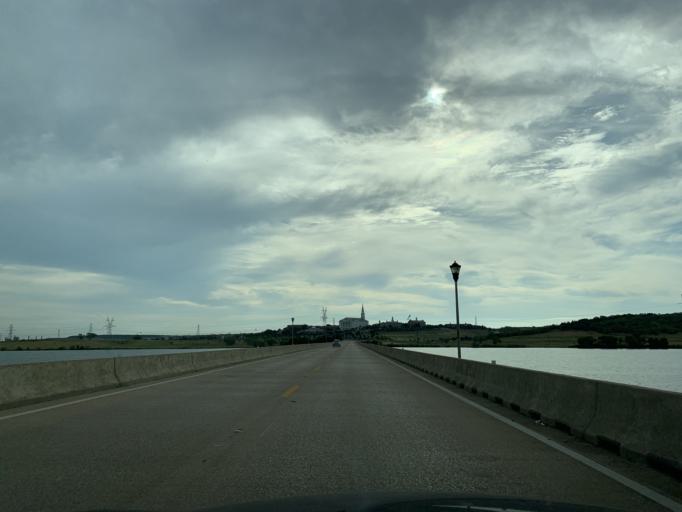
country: US
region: Texas
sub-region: Dallas County
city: Grand Prairie
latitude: 32.7075
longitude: -96.9605
